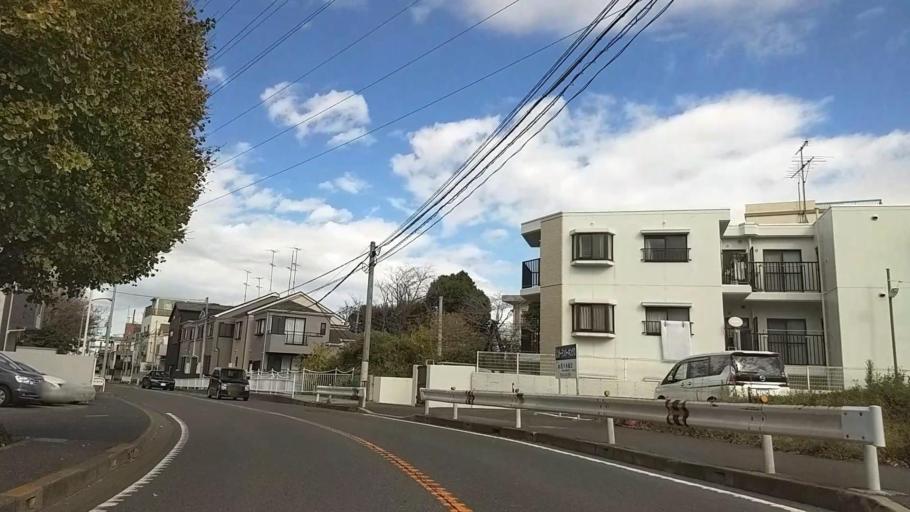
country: JP
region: Kanagawa
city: Yokohama
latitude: 35.4949
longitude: 139.6369
